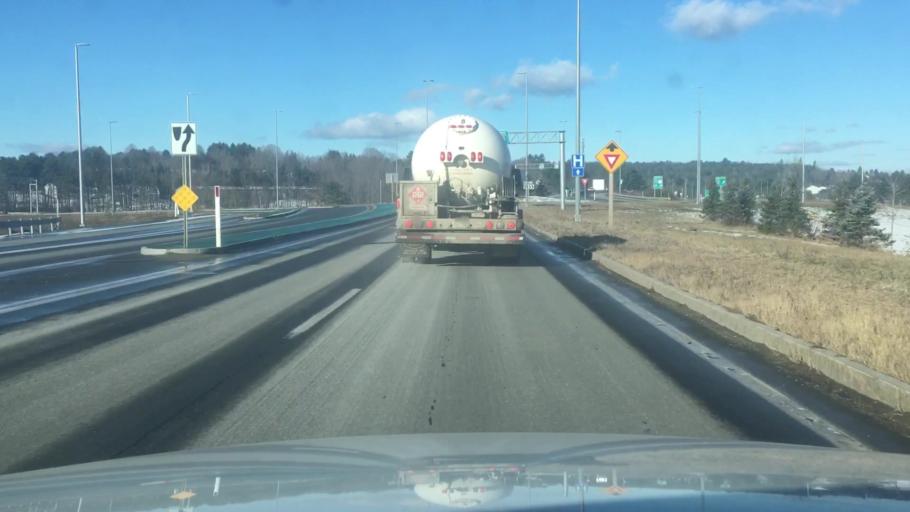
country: US
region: Maine
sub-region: Kennebec County
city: Augusta
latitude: 44.3527
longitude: -69.7796
